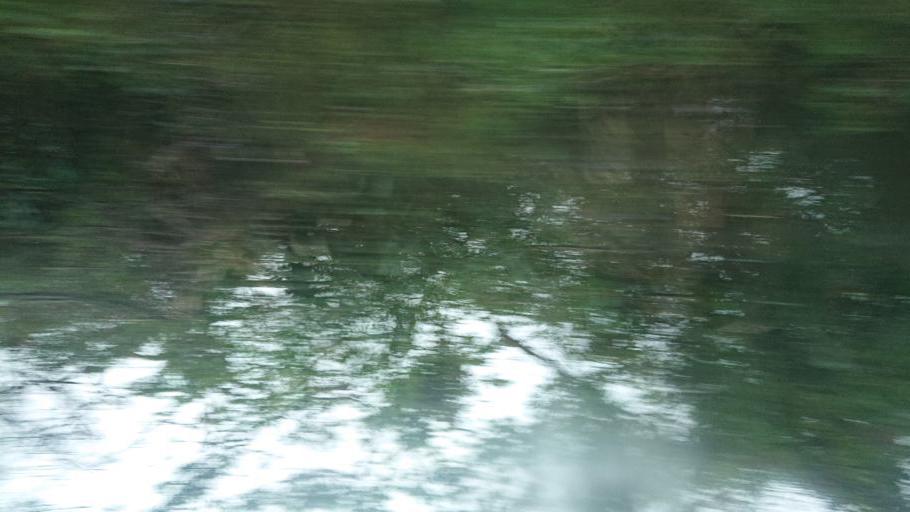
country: TW
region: Taiwan
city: Lugu
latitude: 23.5990
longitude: 120.7135
